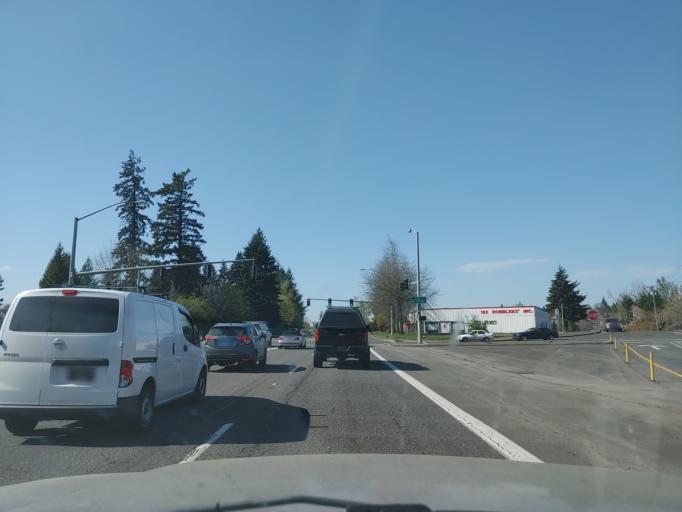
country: US
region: Oregon
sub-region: Clackamas County
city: Milwaukie
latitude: 45.4389
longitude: -122.6243
